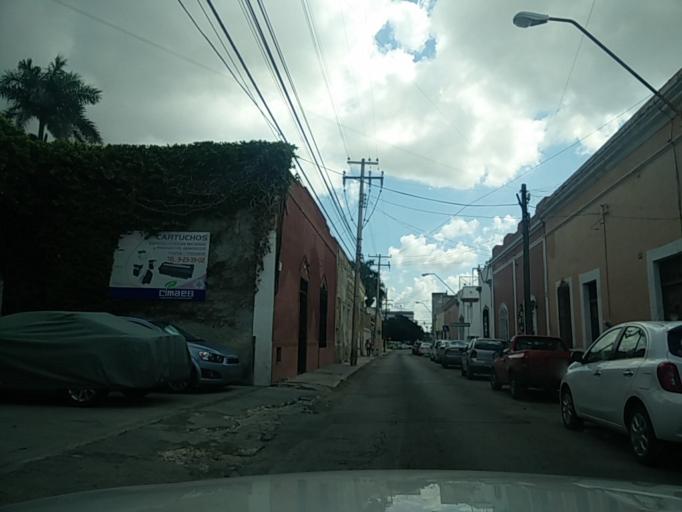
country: MX
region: Yucatan
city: Merida
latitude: 20.9781
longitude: -89.6208
